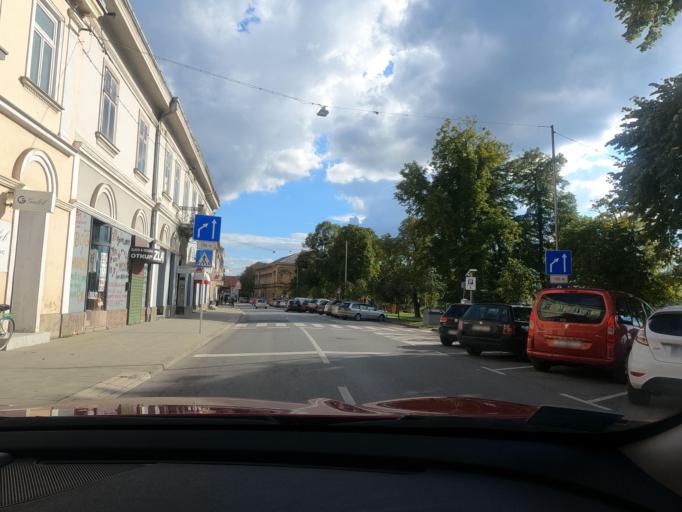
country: HR
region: Sisacko-Moslavacka
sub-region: Grad Sisak
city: Sisak
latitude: 45.4866
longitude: 16.3708
